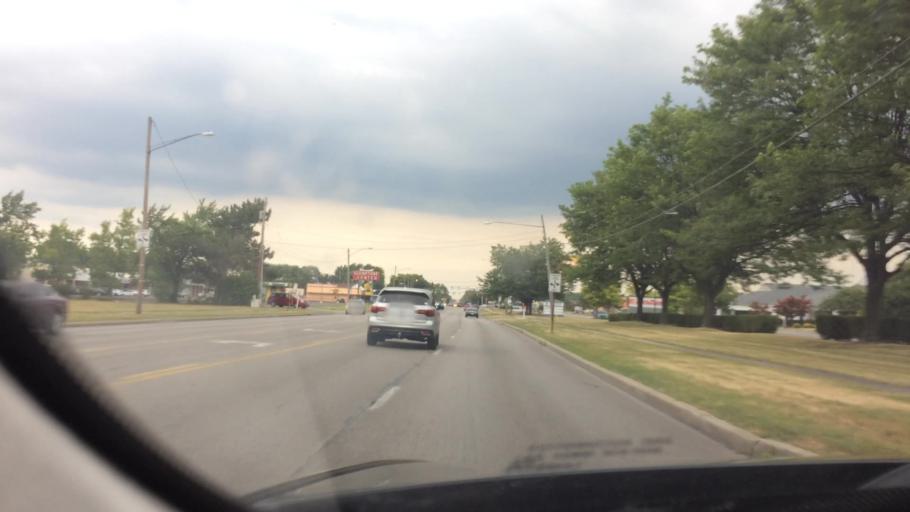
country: US
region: Ohio
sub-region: Wood County
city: Perrysburg
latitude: 41.6089
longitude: -83.6257
